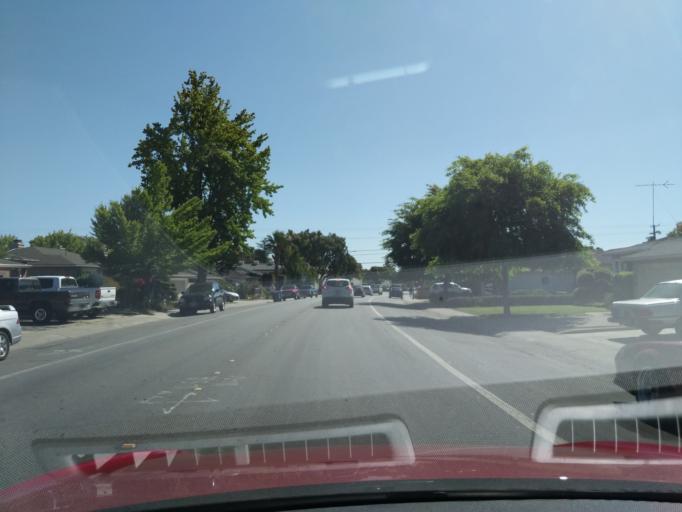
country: US
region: California
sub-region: San Mateo County
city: Belmont
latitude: 37.5334
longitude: -122.3056
